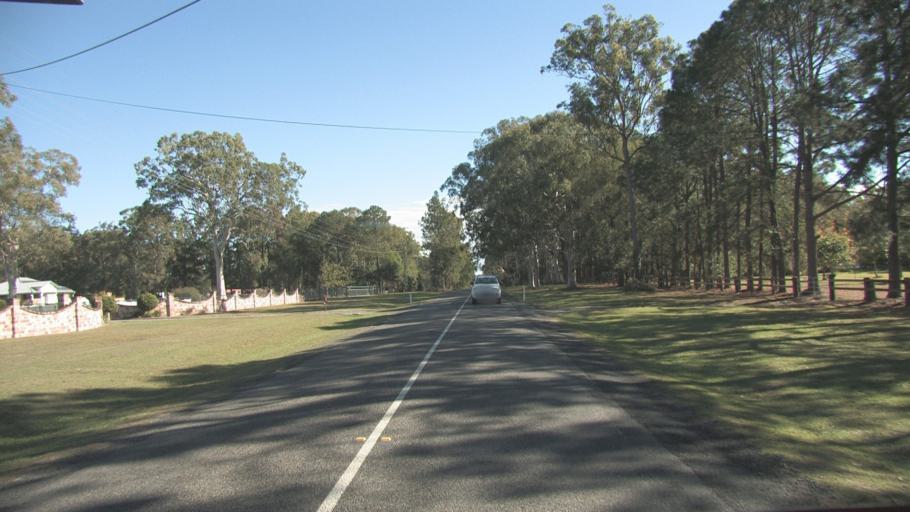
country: AU
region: Queensland
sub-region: Logan
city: Chambers Flat
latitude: -27.7916
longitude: 153.0816
